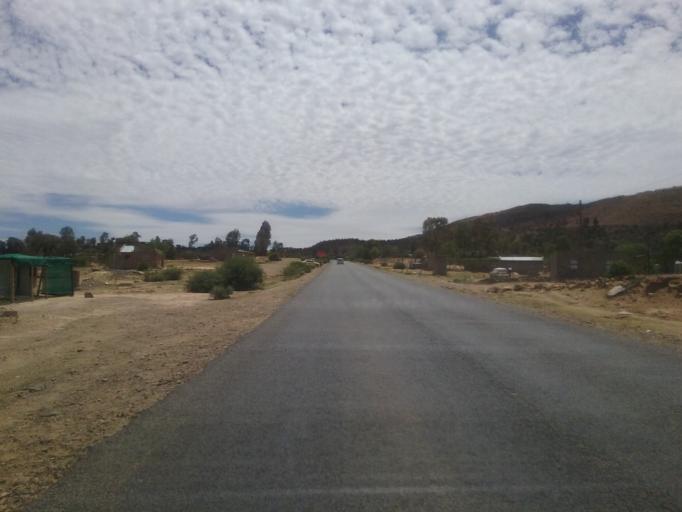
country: LS
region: Mafeteng
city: Mafeteng
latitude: -29.8430
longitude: 27.2306
